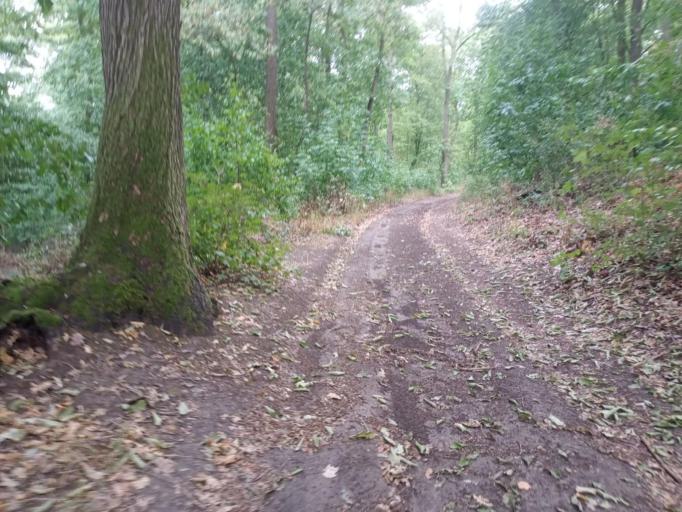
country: HU
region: Pest
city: Pilisborosjeno
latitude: 47.6227
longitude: 19.0031
